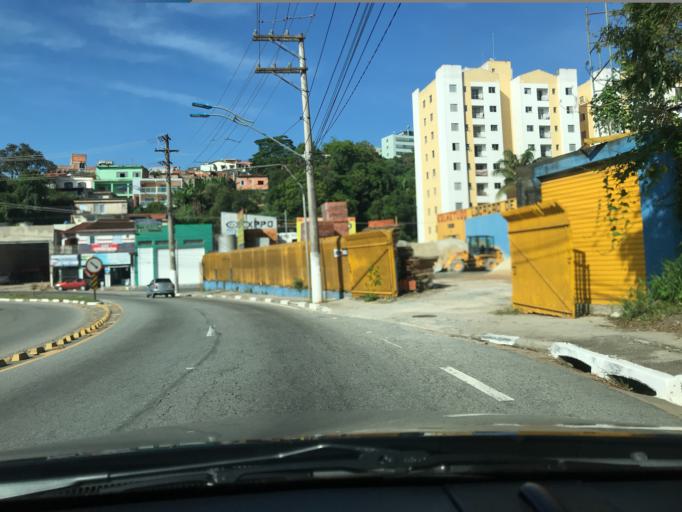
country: BR
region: Sao Paulo
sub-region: Itapevi
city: Itapevi
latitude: -23.5357
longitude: -46.9399
